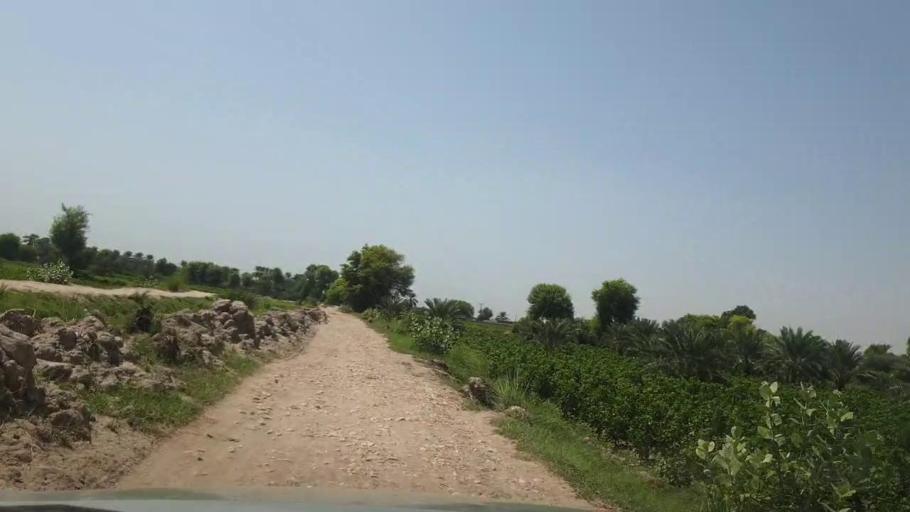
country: PK
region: Sindh
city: Rohri
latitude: 27.6500
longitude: 68.9841
